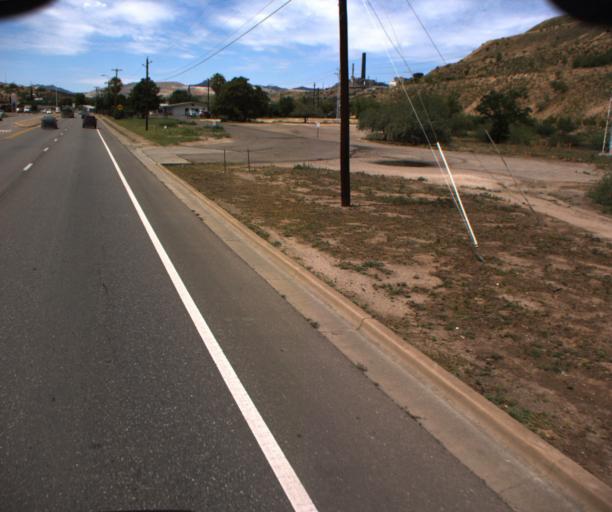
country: US
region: Arizona
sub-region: Gila County
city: Claypool
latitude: 33.4125
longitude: -110.8405
